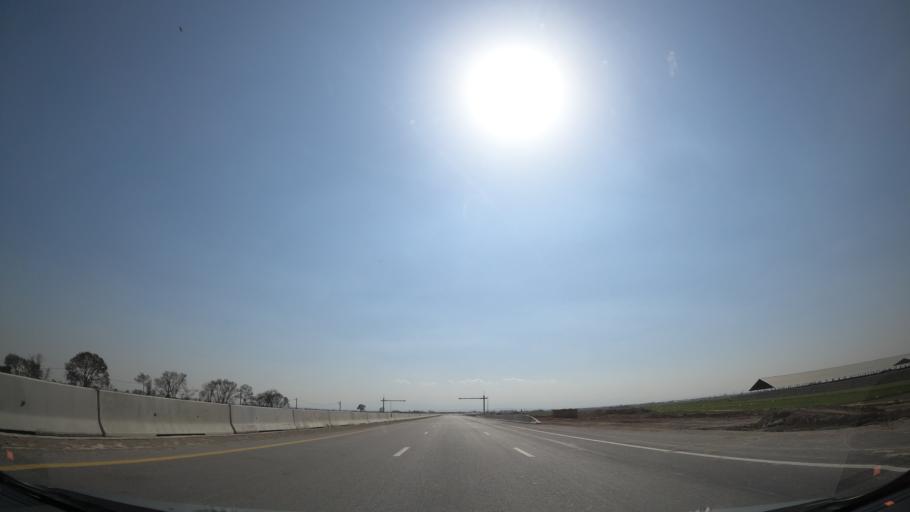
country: IR
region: Qazvin
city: Abyek
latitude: 35.9916
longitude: 50.4620
